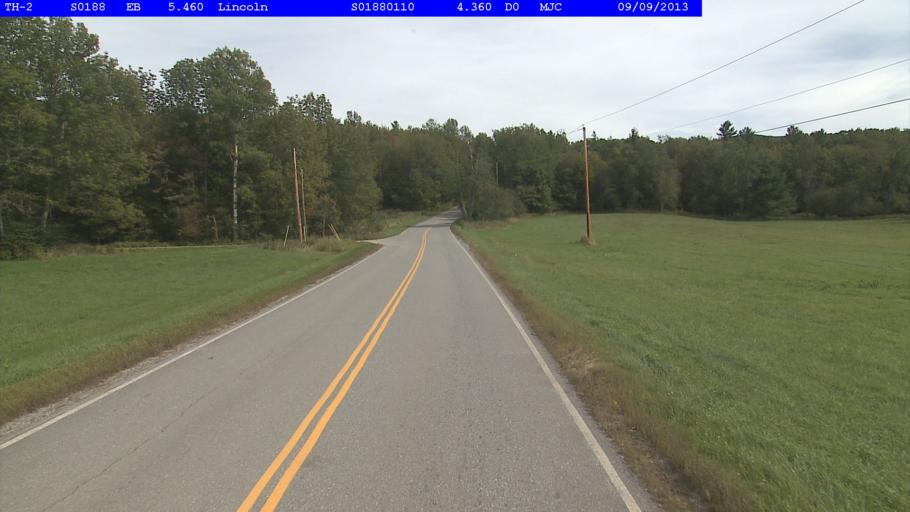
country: US
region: Vermont
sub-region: Addison County
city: Bristol
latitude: 44.0960
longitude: -72.9651
